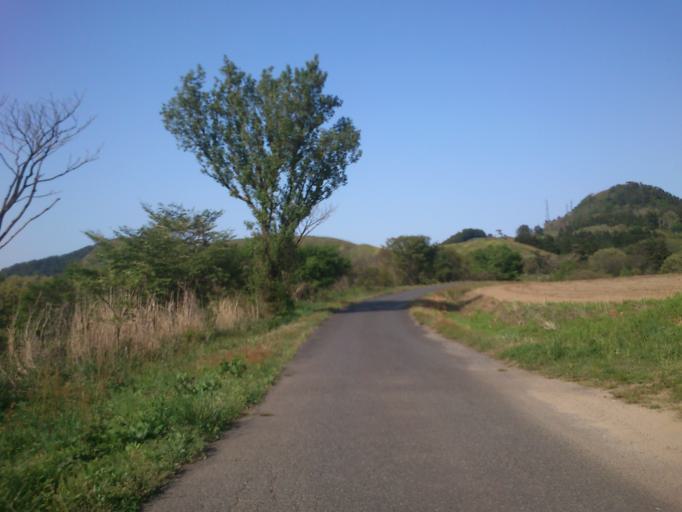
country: JP
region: Kyoto
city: Miyazu
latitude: 35.7215
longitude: 135.1906
